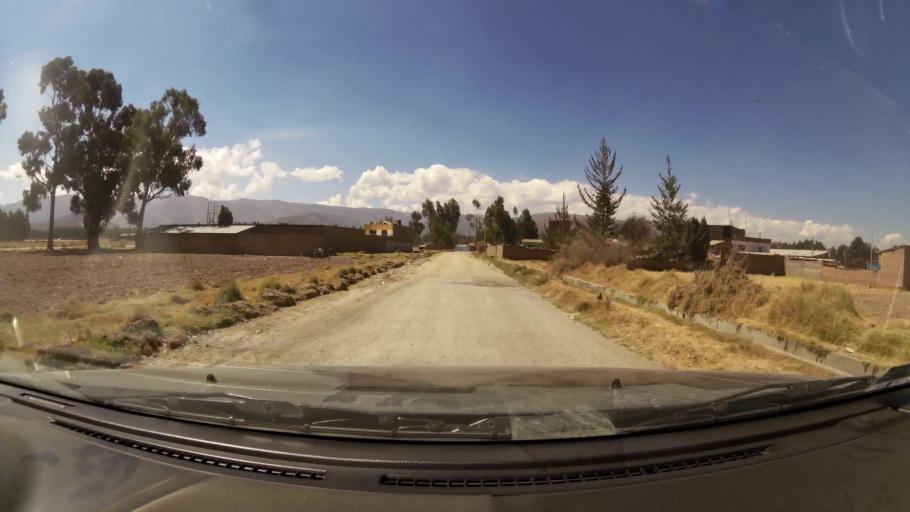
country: PE
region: Junin
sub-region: Provincia de Jauja
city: Jauja
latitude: -11.7674
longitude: -75.4947
